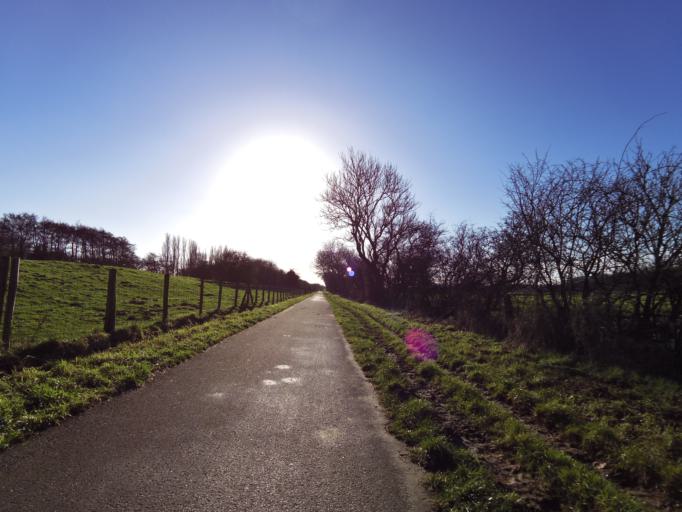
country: NL
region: South Holland
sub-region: Gemeente Hellevoetsluis
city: Nieuw-Helvoet
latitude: 51.8947
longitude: 4.0700
